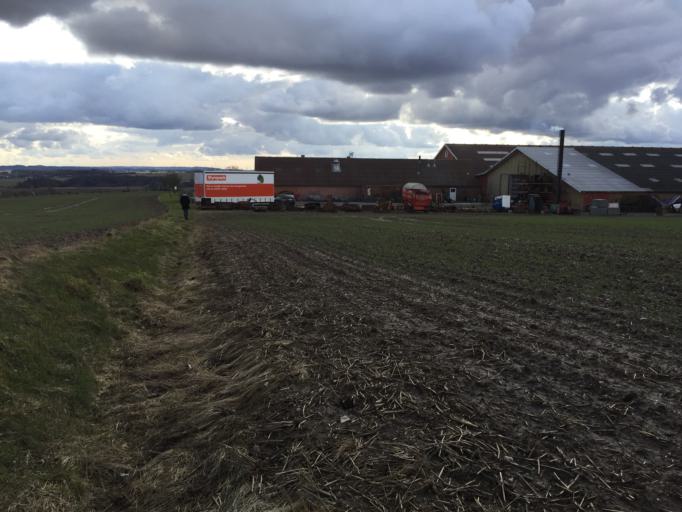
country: DK
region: Central Jutland
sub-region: Skanderborg Kommune
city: Ry
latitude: 56.1810
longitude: 9.7905
